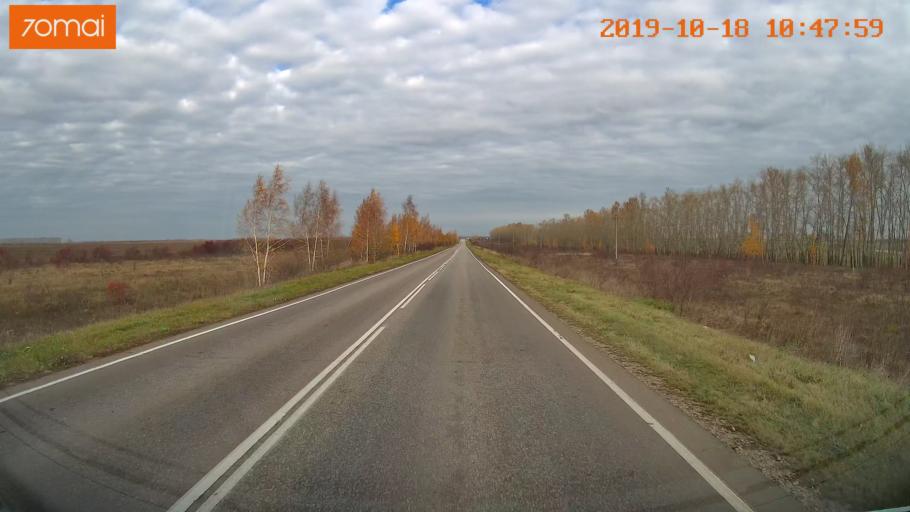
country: RU
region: Tula
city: Yepifan'
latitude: 53.7095
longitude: 38.6974
